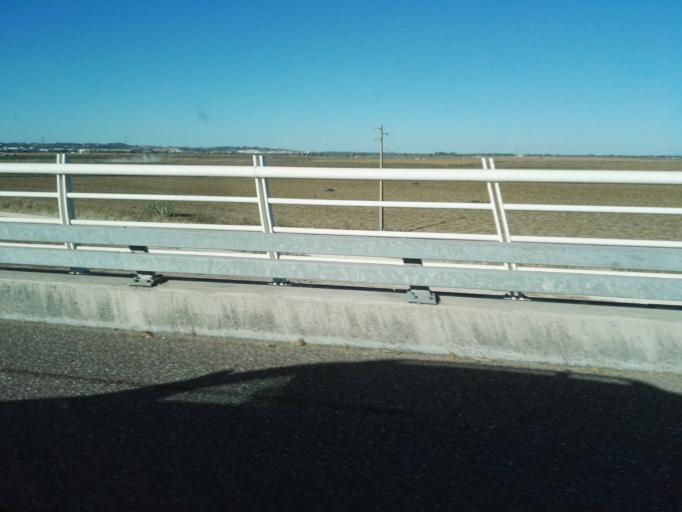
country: PT
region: Lisbon
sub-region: Vila Franca de Xira
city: Castanheira do Ribatejo
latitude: 39.0026
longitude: -8.9075
